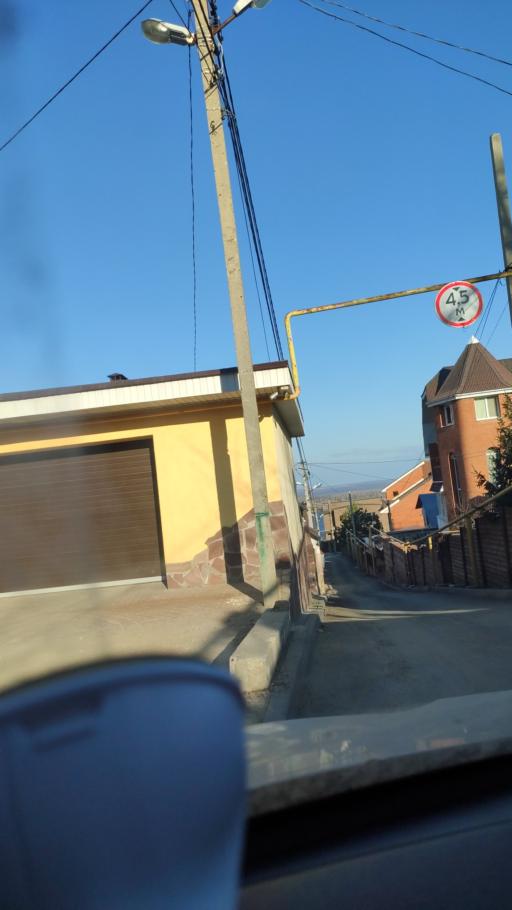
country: RU
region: Samara
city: Samara
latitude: 53.2297
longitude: 50.1585
